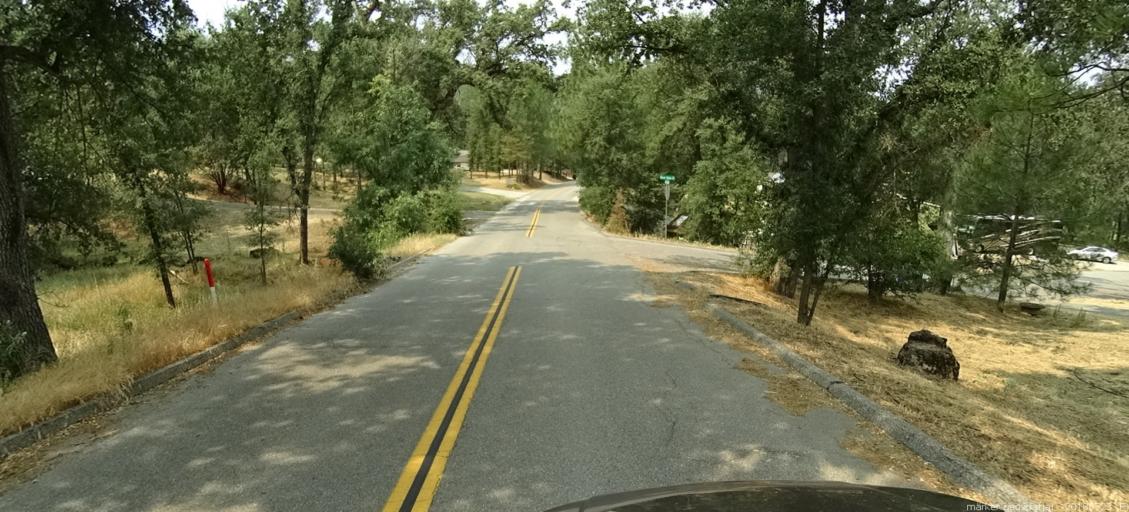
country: US
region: California
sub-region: Madera County
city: Ahwahnee
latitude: 37.3346
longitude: -119.7033
